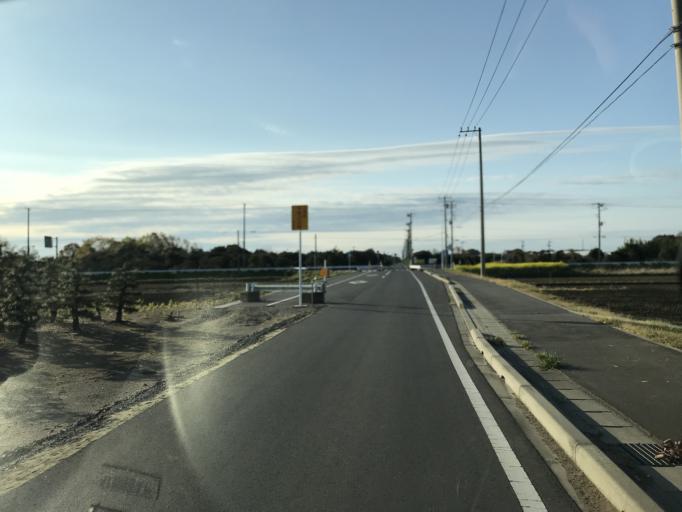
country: JP
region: Chiba
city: Yokaichiba
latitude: 35.6723
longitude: 140.5850
